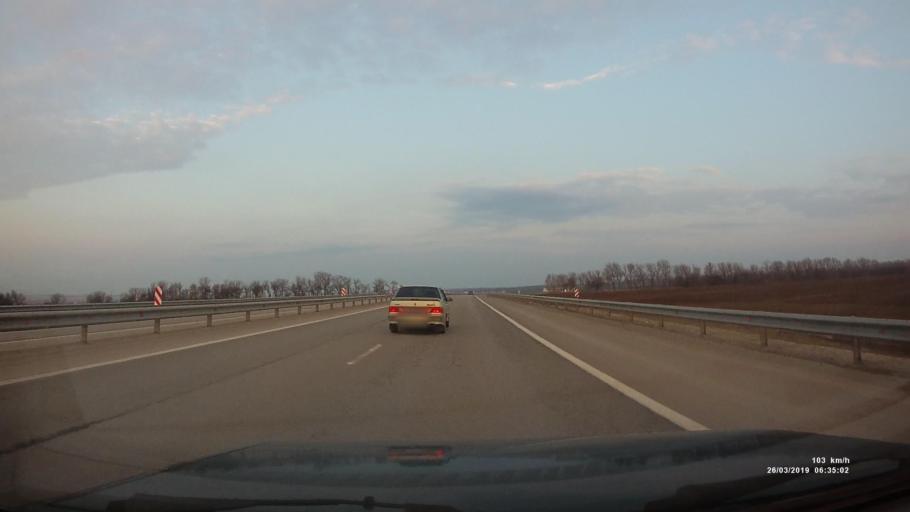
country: RU
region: Rostov
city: Chaltyr
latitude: 47.2788
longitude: 39.4544
